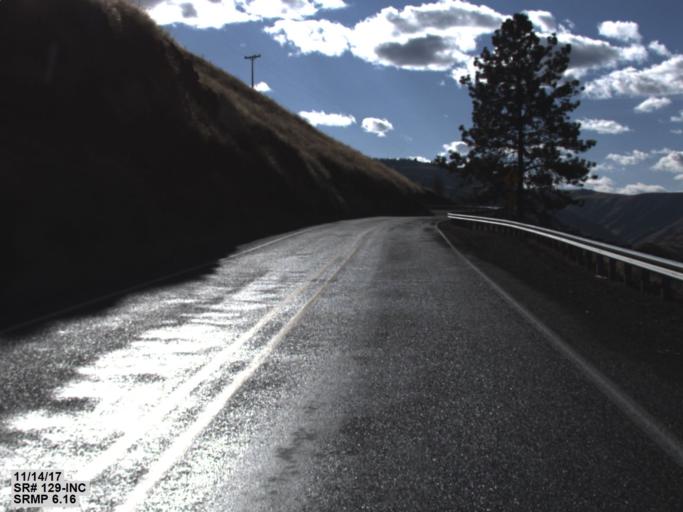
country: US
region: Washington
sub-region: Asotin County
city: Asotin
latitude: 46.0521
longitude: -117.2383
